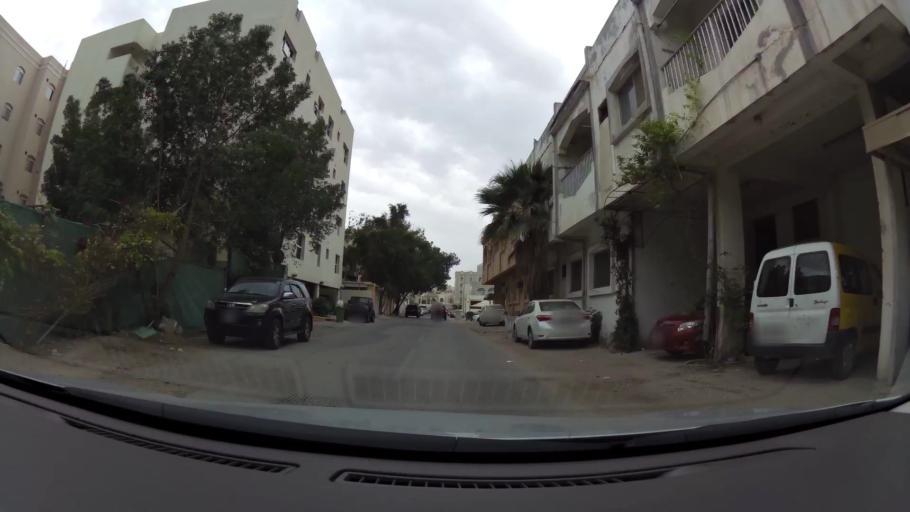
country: QA
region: Baladiyat ad Dawhah
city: Doha
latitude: 25.2761
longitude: 51.5066
